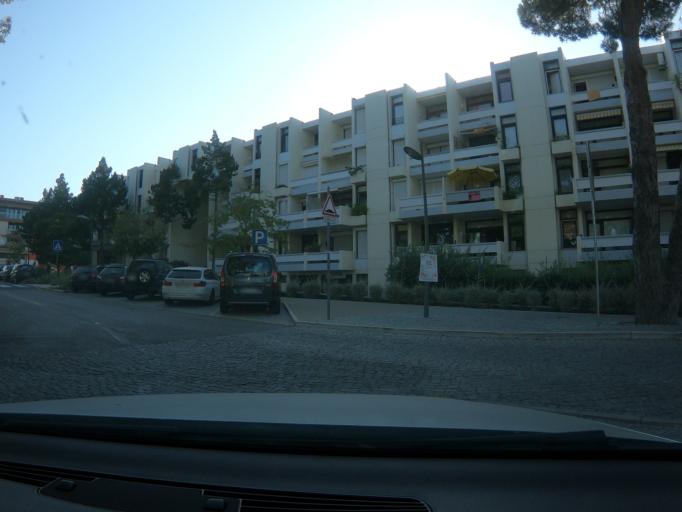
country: PT
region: Setubal
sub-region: Setubal
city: Setubal
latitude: 38.4927
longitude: -8.9012
